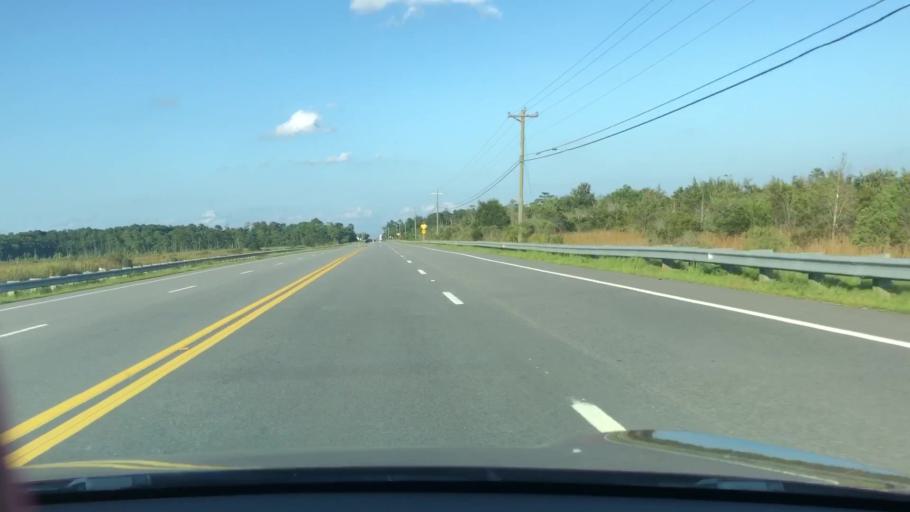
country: US
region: North Carolina
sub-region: Dare County
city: Manteo
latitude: 35.8802
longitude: -75.7735
